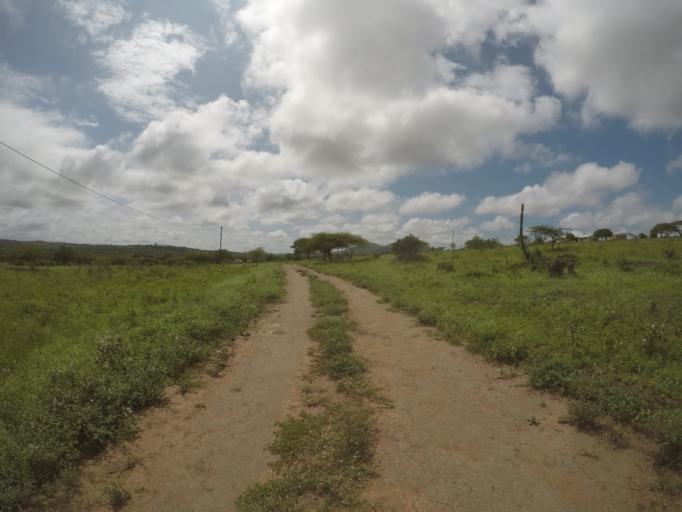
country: ZA
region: KwaZulu-Natal
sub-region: uThungulu District Municipality
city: Empangeni
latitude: -28.5720
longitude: 31.8429
